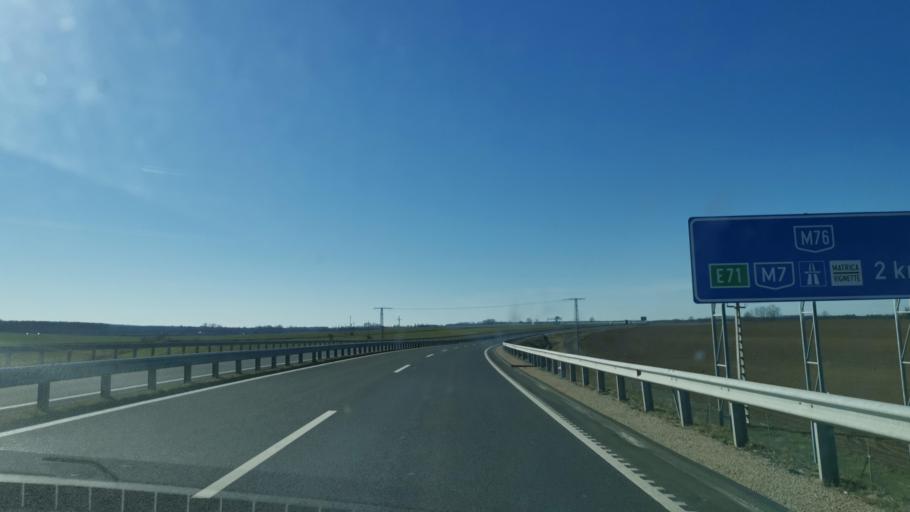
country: HU
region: Somogy
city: Balatonbereny
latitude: 46.6666
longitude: 17.2995
